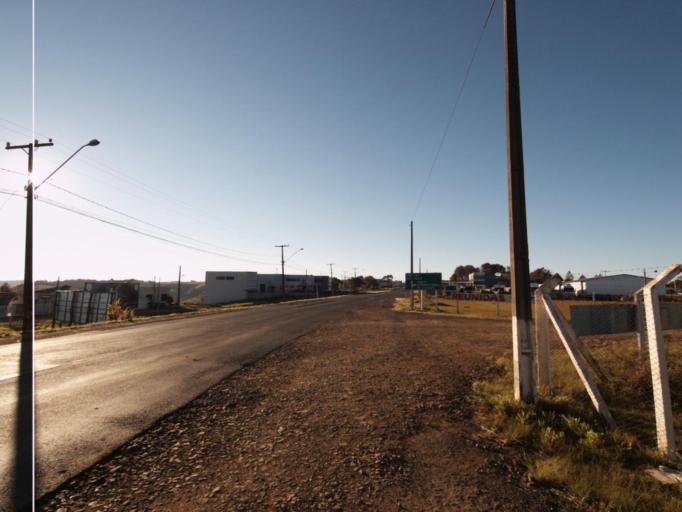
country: AR
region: Misiones
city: Bernardo de Irigoyen
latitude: -26.2571
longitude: -53.6206
